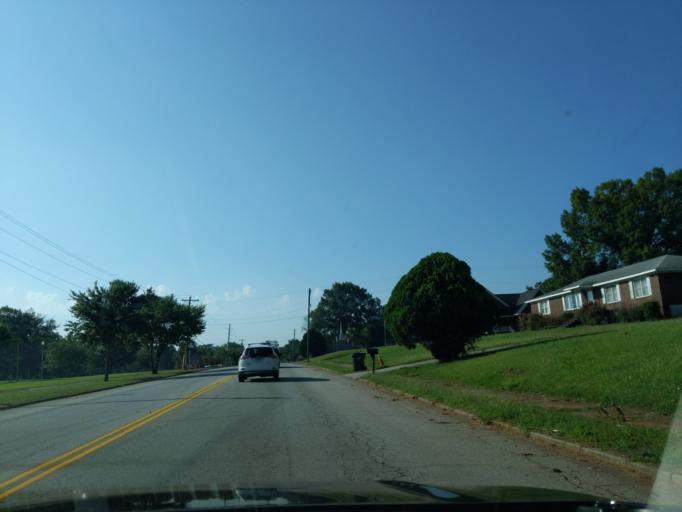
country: US
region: South Carolina
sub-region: Newberry County
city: Prosperity
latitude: 34.2150
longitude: -81.5381
